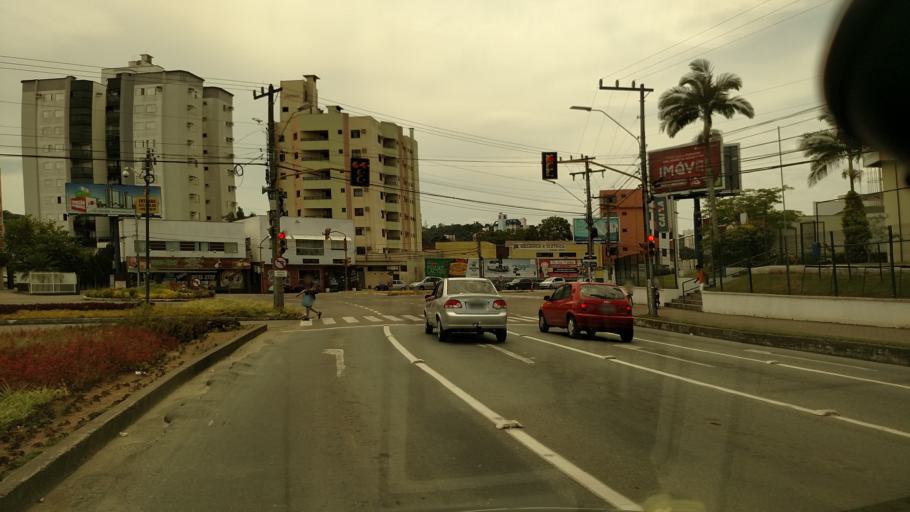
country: BR
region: Santa Catarina
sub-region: Blumenau
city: Blumenau
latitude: -26.9126
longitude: -49.0806
